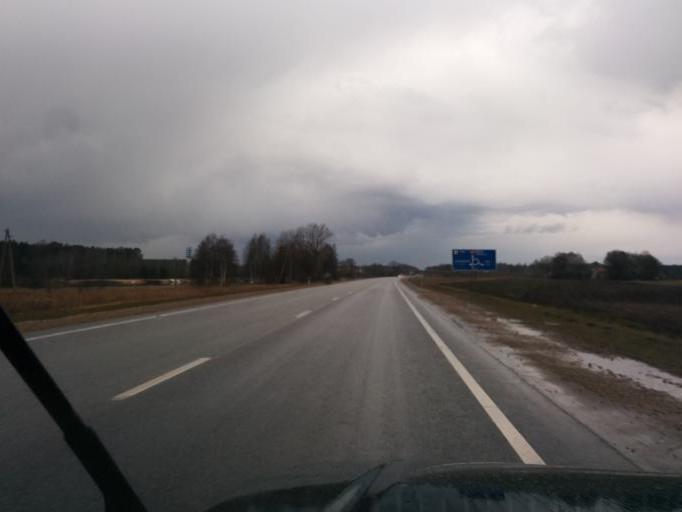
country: LV
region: Babite
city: Pinki
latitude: 56.8730
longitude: 23.9604
